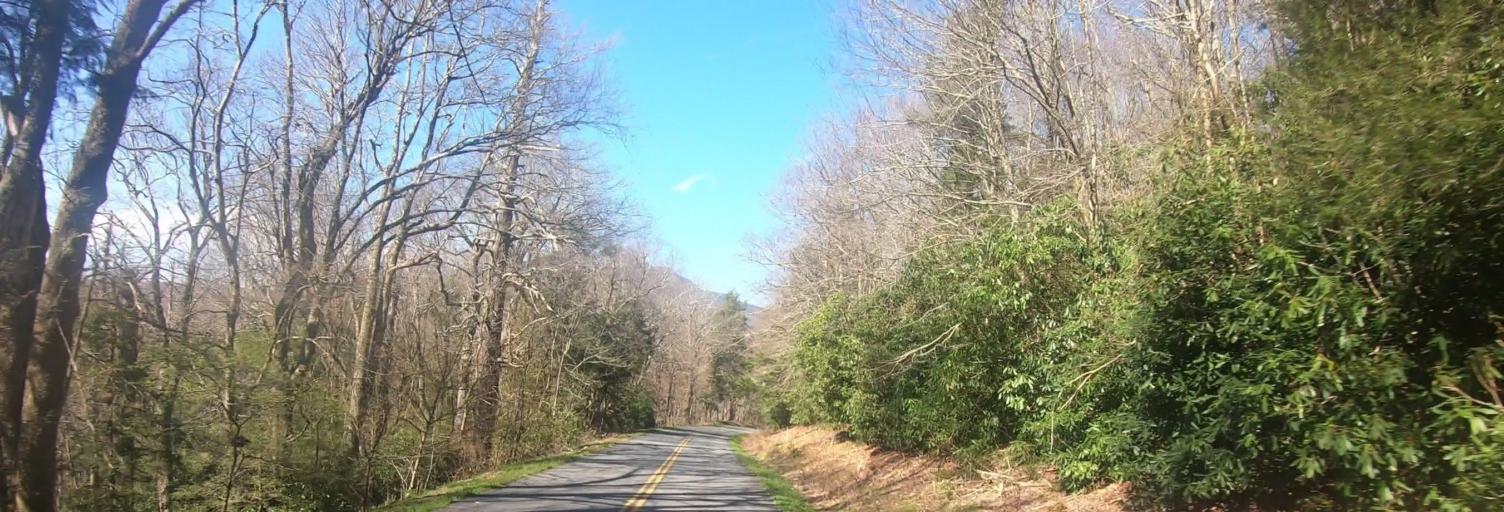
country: US
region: North Carolina
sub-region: Avery County
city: Newland
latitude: 36.0696
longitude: -81.8403
